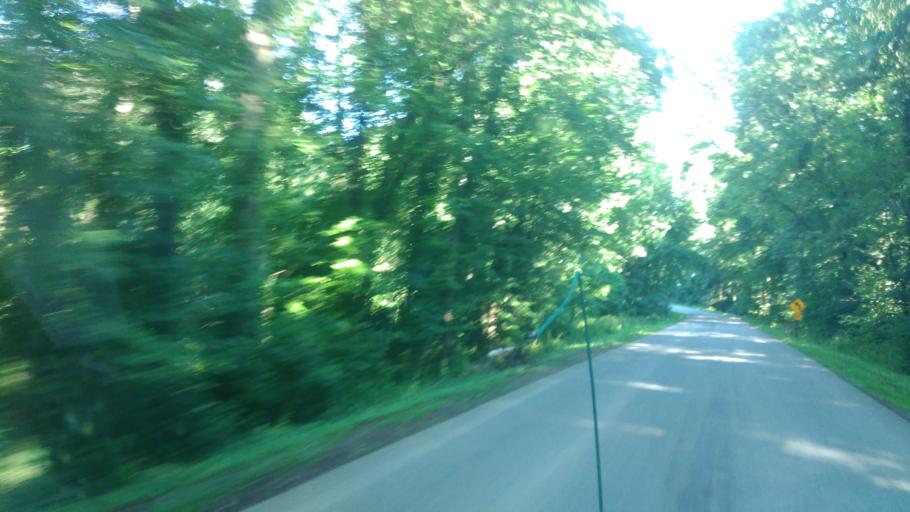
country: US
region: New York
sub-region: Wayne County
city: Sodus
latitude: 43.1914
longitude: -77.0816
